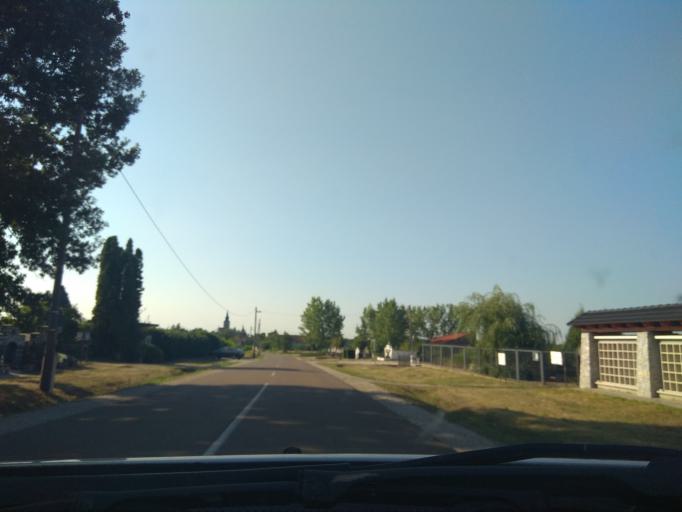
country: HU
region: Borsod-Abauj-Zemplen
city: Emod
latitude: 47.9513
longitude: 20.8098
